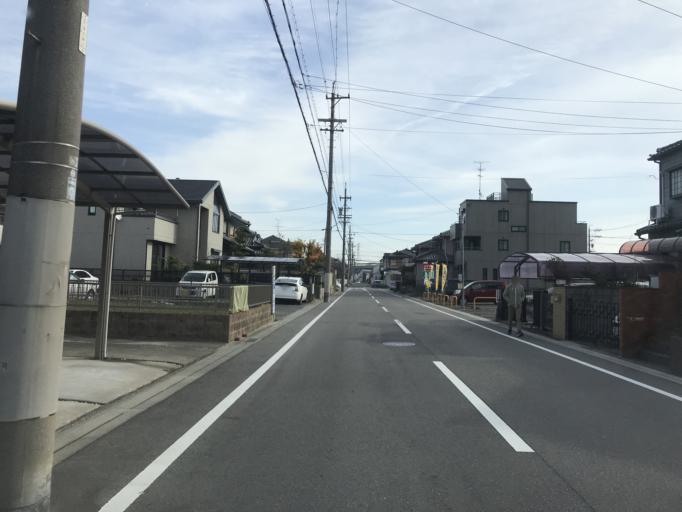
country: JP
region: Aichi
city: Inazawa
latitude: 35.2204
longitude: 136.8297
